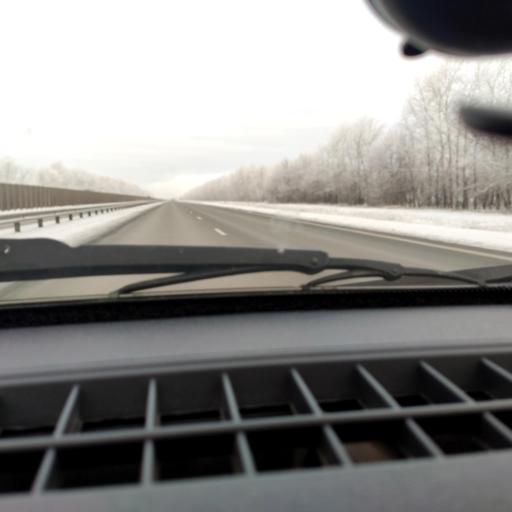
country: RU
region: Bashkortostan
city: Kushnarenkovo
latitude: 55.0333
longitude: 55.4600
